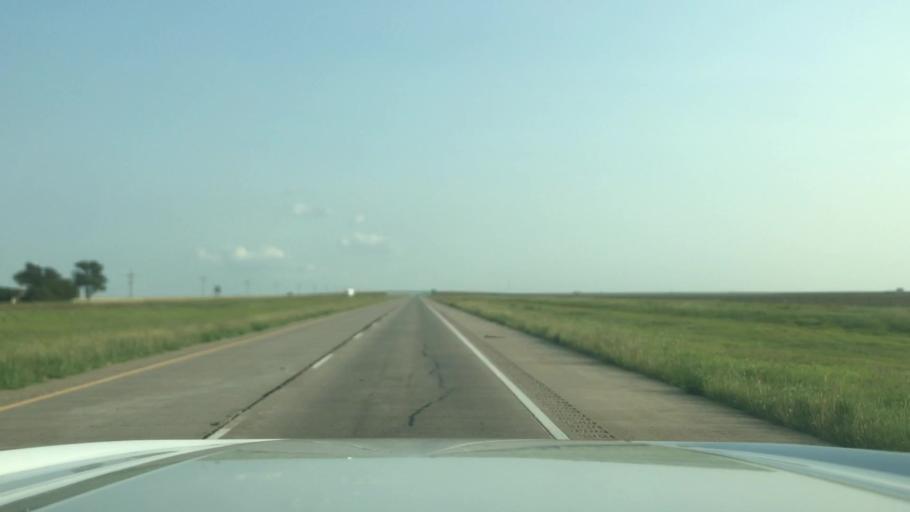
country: US
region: Texas
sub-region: Randall County
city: Canyon
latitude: 34.8973
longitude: -101.8488
